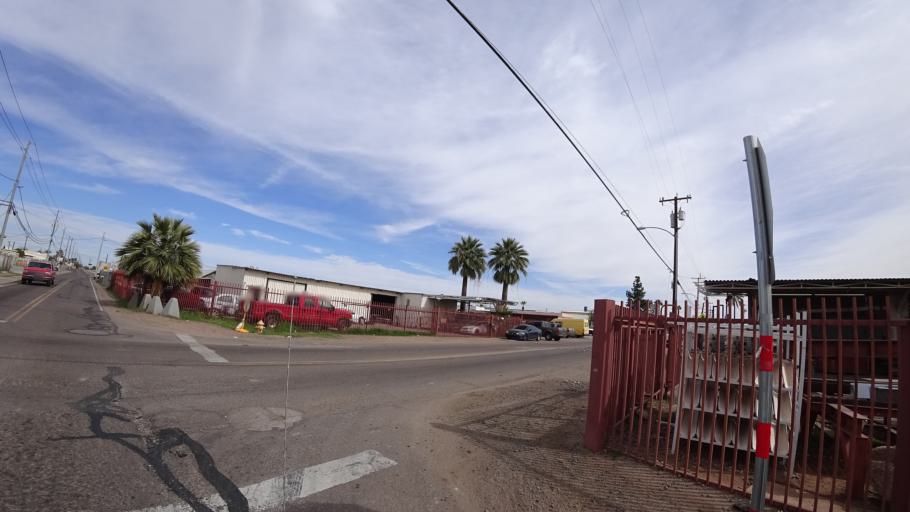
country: US
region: Arizona
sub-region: Maricopa County
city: Phoenix
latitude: 33.4421
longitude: -112.1260
